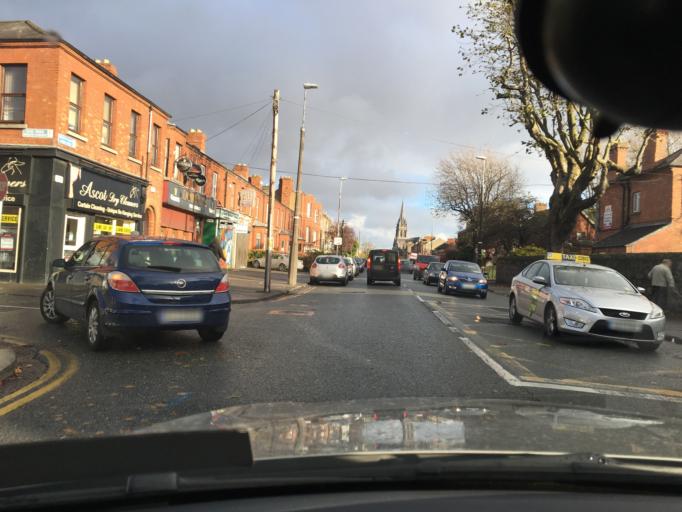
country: IE
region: Leinster
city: Cabra
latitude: 53.3611
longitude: -6.2835
